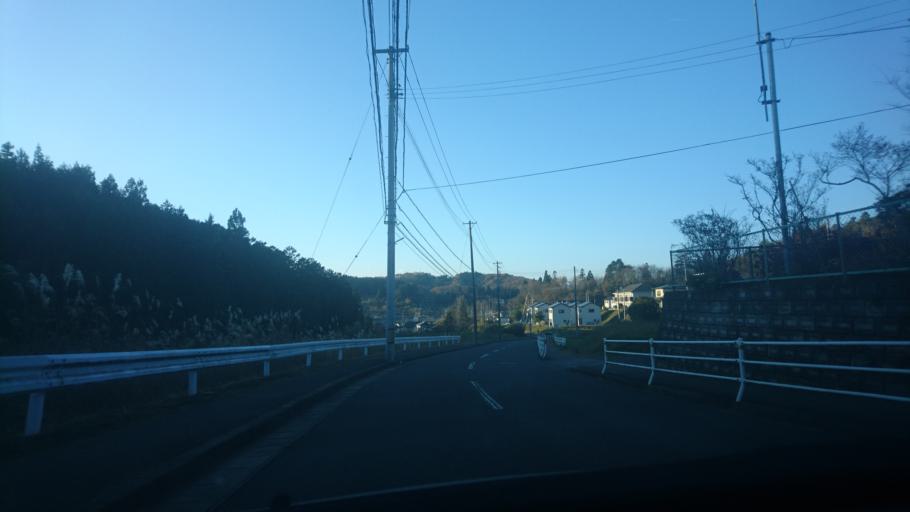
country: JP
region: Iwate
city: Ichinoseki
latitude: 38.9082
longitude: 141.1371
